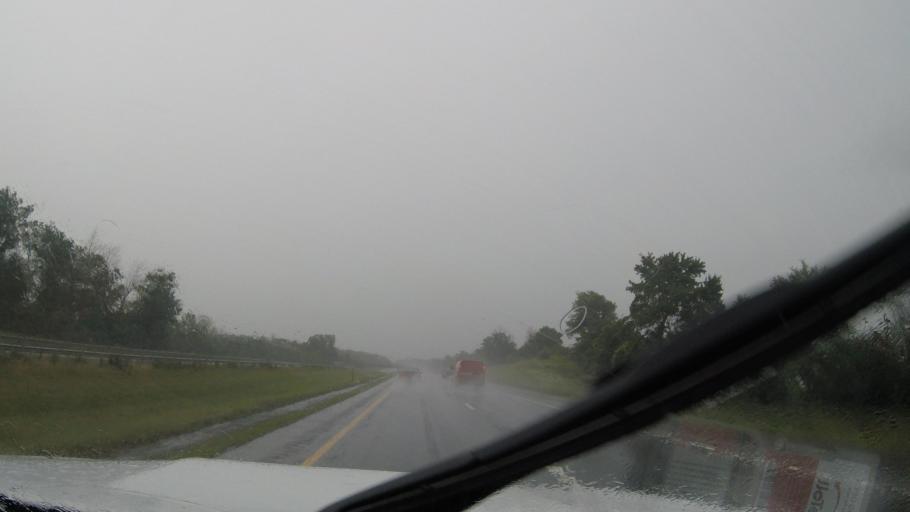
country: US
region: New York
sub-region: Seneca County
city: Seneca Falls
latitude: 42.9688
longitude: -76.8333
